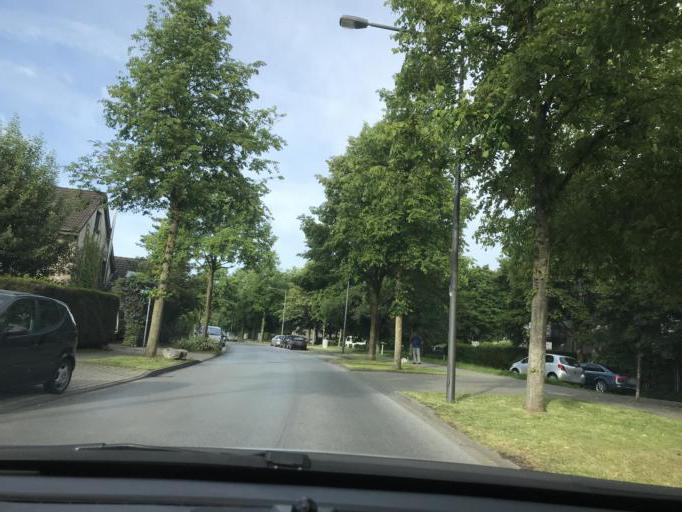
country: DE
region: North Rhine-Westphalia
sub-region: Regierungsbezirk Koln
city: Wurselen
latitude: 50.7480
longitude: 6.1497
